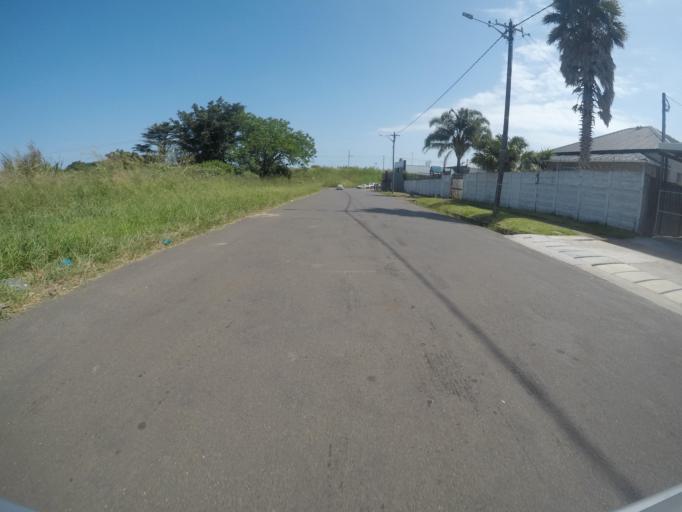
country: ZA
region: Eastern Cape
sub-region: Buffalo City Metropolitan Municipality
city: East London
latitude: -32.9701
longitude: 27.8784
